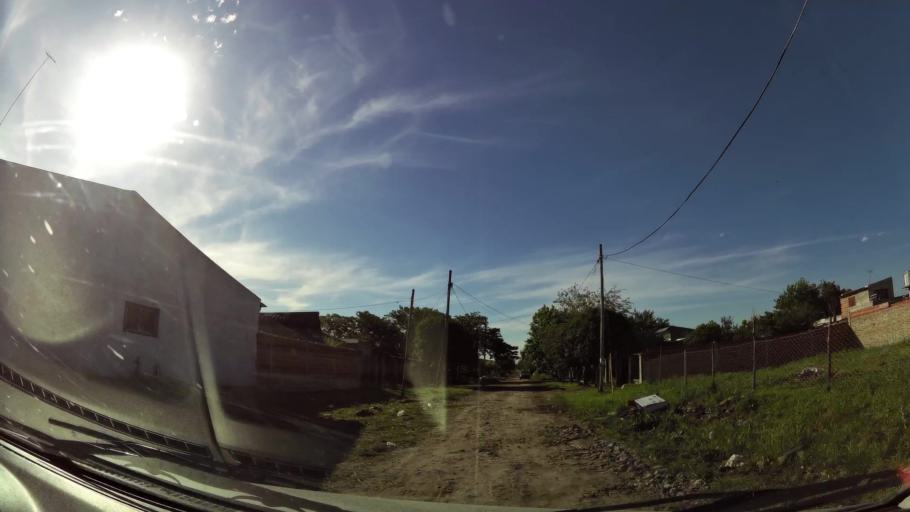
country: AR
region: Buenos Aires
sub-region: Partido de Florencio Varela
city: Florencio Varela
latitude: -34.8285
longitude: -58.3562
